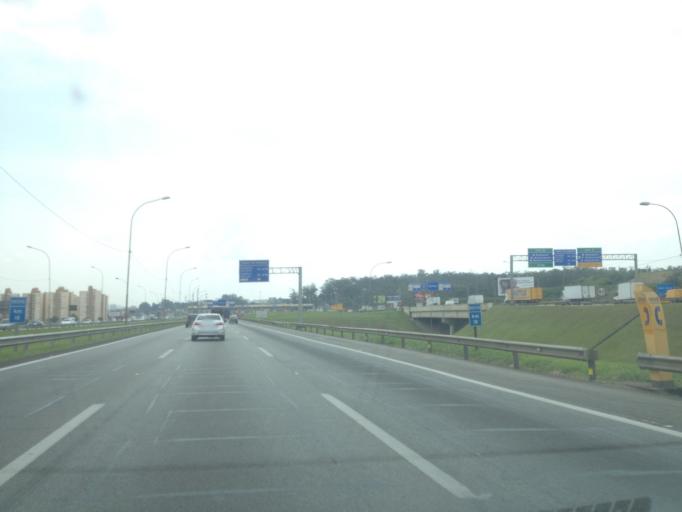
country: BR
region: Sao Paulo
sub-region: Osasco
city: Osasco
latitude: -23.5147
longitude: -46.7950
